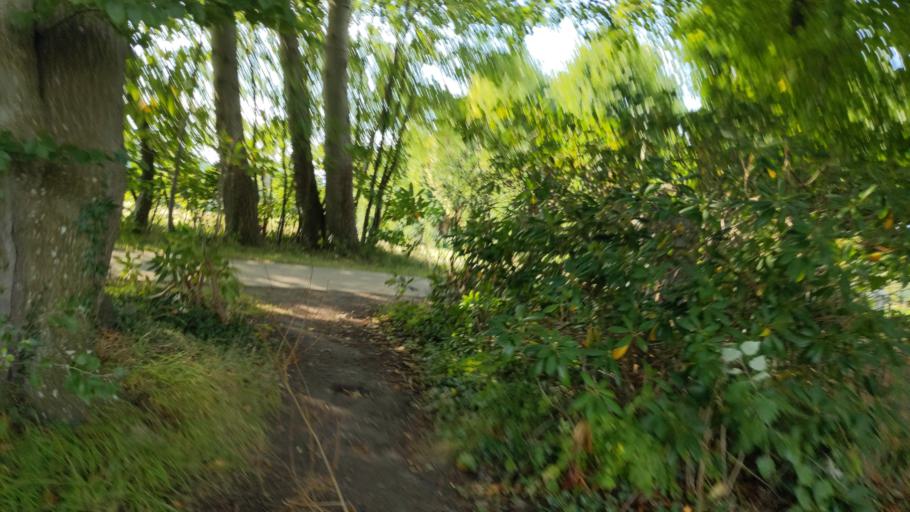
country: DE
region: Mecklenburg-Vorpommern
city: Kalkhorst
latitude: 53.9922
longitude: 11.0102
